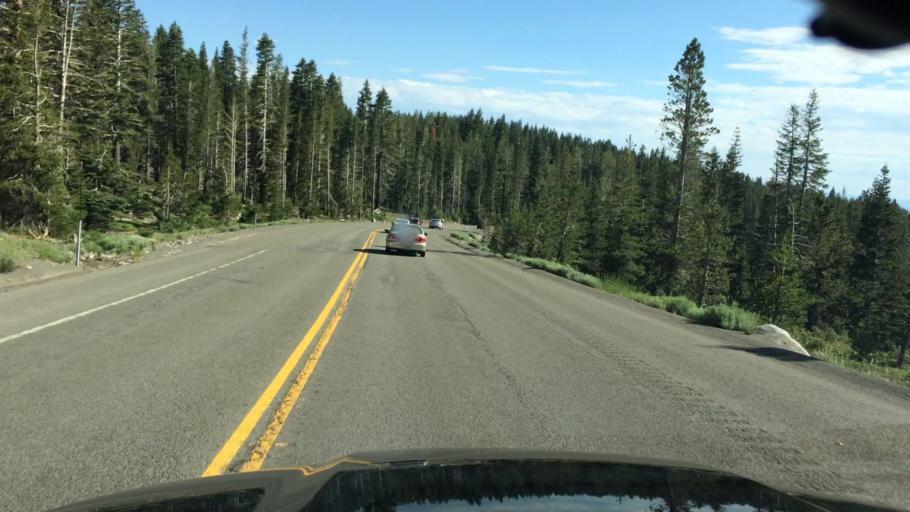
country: US
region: Nevada
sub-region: Washoe County
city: Incline Village
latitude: 39.2906
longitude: -119.9259
